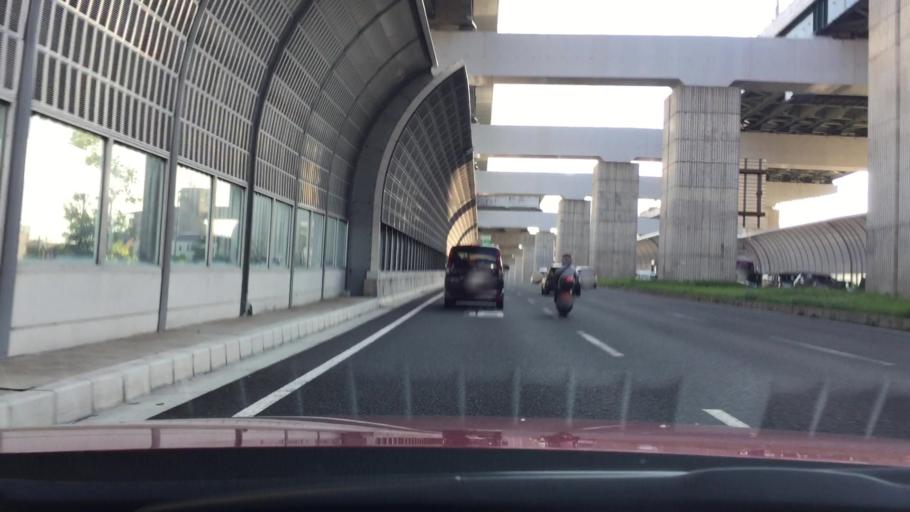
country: JP
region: Osaka
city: Kadoma
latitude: 34.7171
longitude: 135.5920
